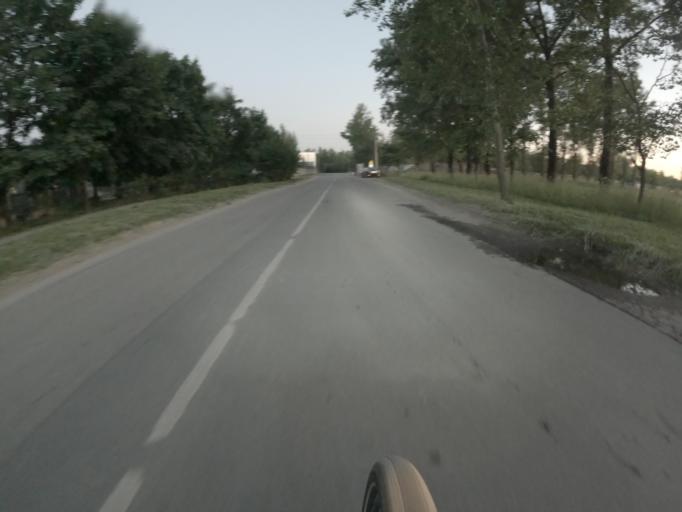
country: RU
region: St.-Petersburg
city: Sapernyy
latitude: 59.7780
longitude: 30.6910
